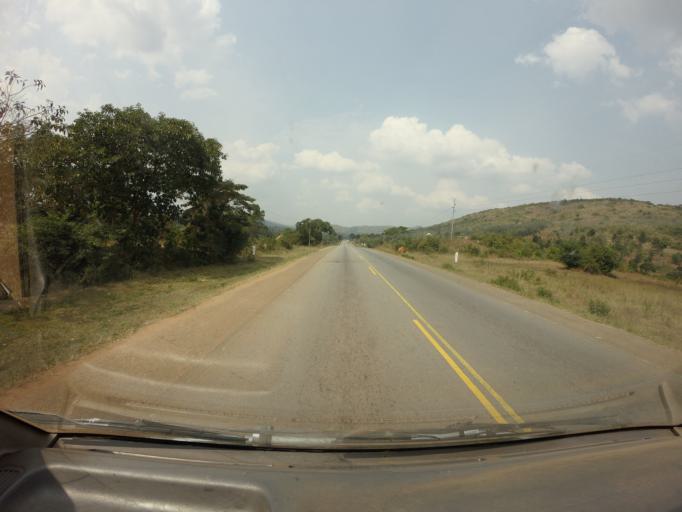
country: UG
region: Central Region
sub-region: Lyantonde District
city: Lyantonde
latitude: -0.3805
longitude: 31.2371
